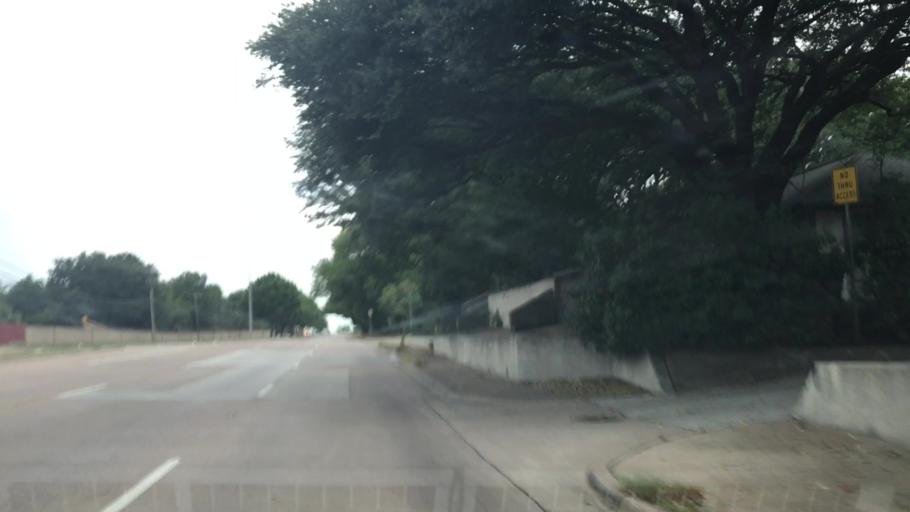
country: US
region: Texas
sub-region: Dallas County
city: Addison
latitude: 32.9501
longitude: -96.7863
